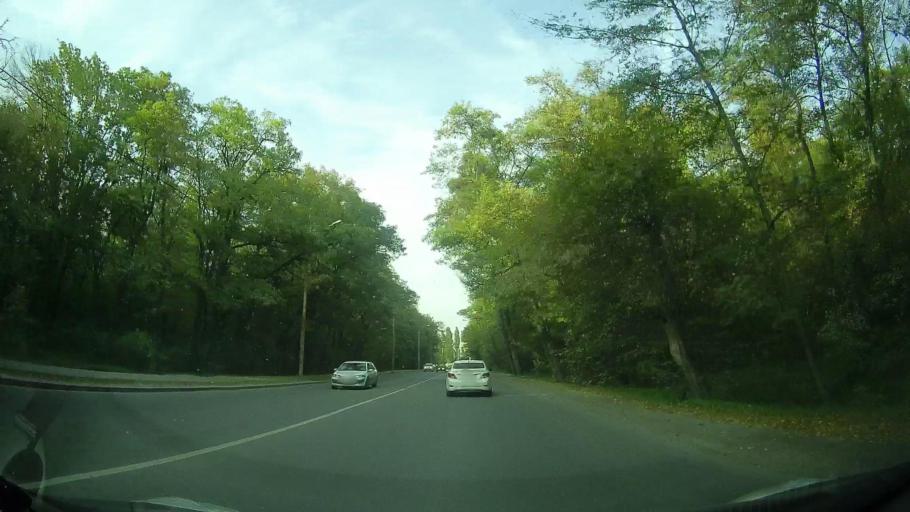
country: RU
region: Rostov
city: Imeni Chkalova
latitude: 47.2762
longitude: 39.7959
